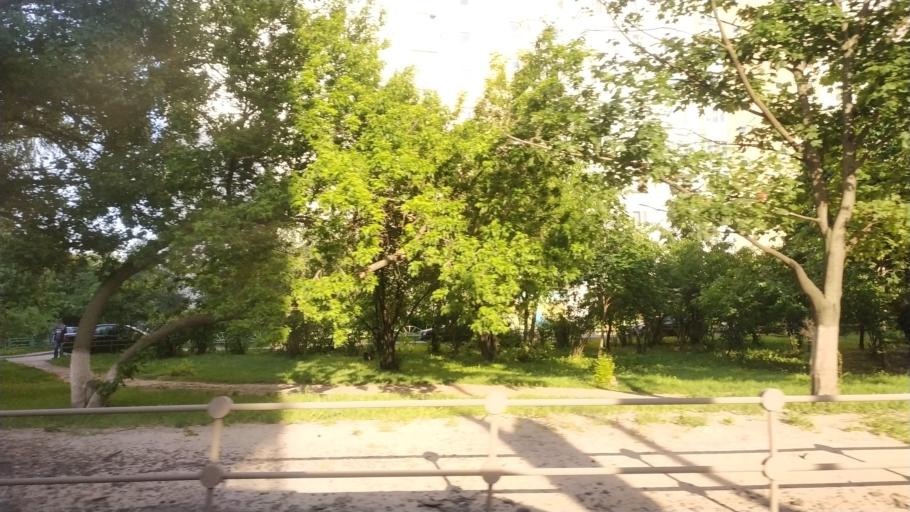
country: RU
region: Moskovskaya
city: Saltykovka
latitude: 55.7291
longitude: 37.9622
